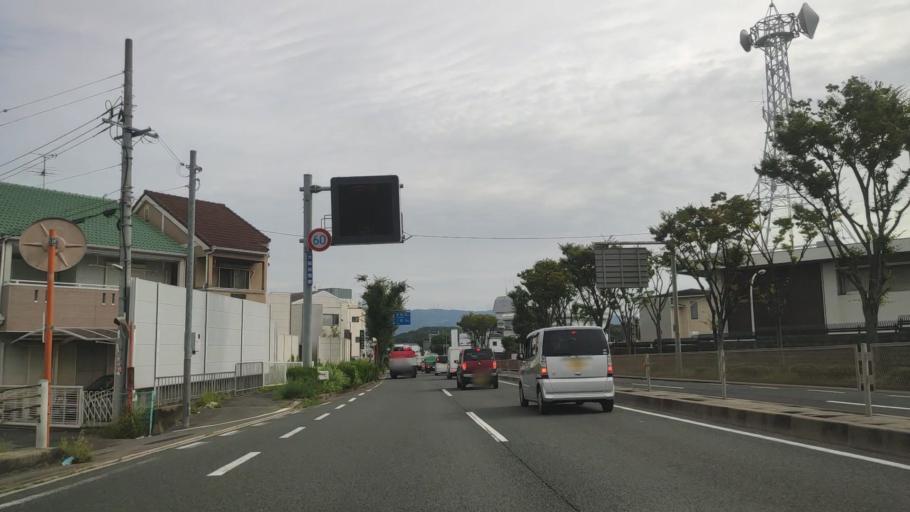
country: JP
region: Osaka
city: Kashihara
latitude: 34.5631
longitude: 135.6026
